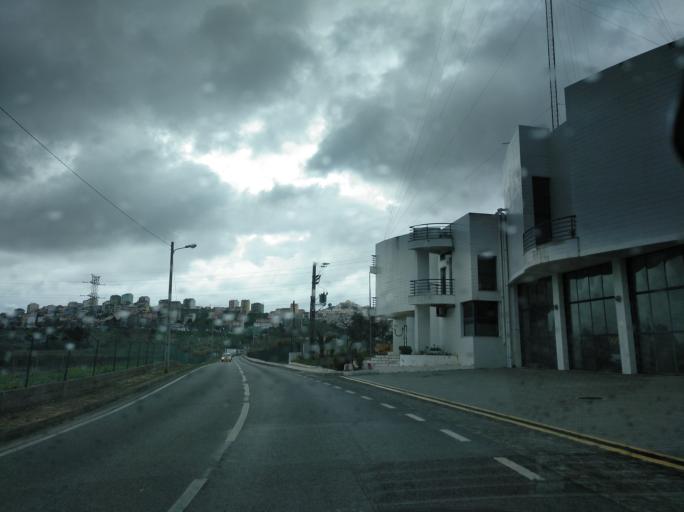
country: PT
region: Lisbon
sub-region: Odivelas
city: Pontinha
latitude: 38.7747
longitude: -9.2084
